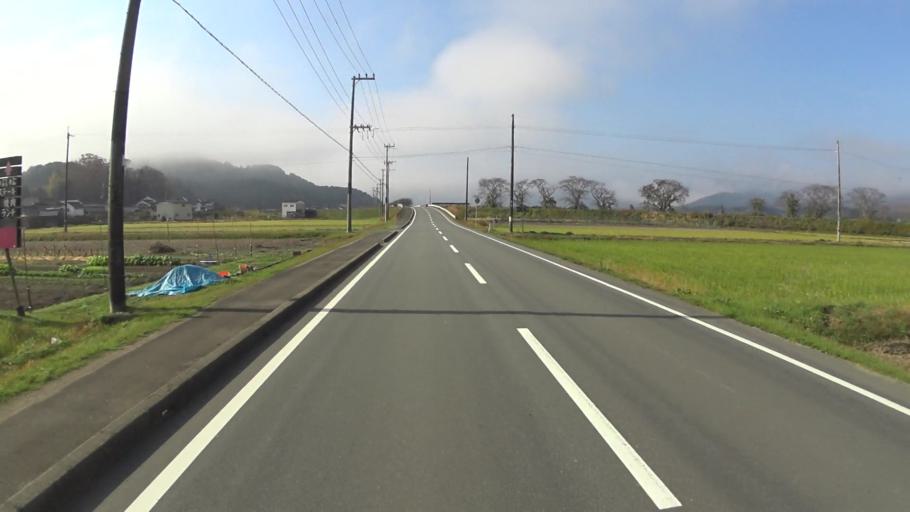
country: JP
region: Kyoto
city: Fukuchiyama
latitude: 35.2494
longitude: 135.1589
